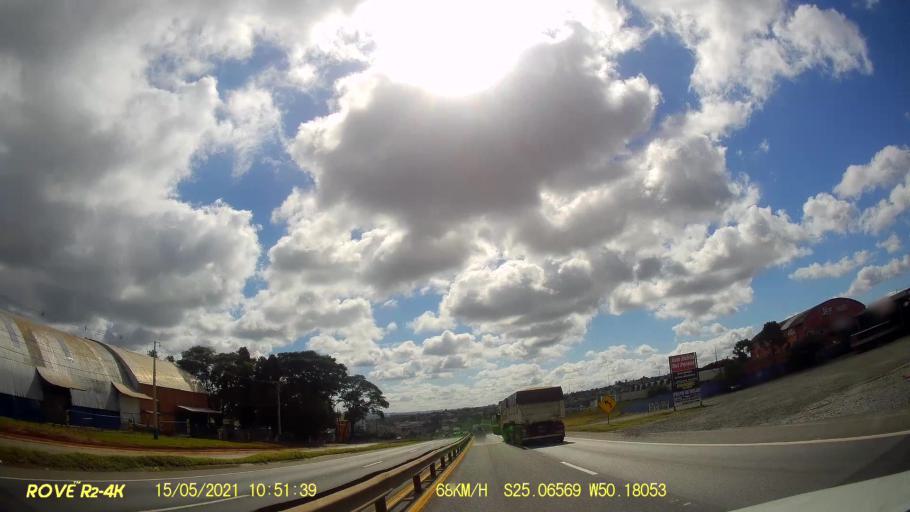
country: BR
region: Parana
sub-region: Ponta Grossa
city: Ponta Grossa
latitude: -25.0655
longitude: -50.1810
